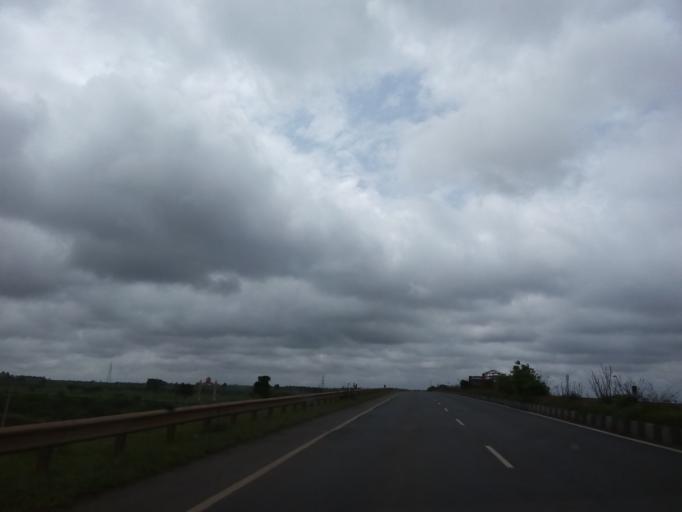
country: IN
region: Karnataka
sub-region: Haveri
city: Haveri
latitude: 14.8401
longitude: 75.3520
